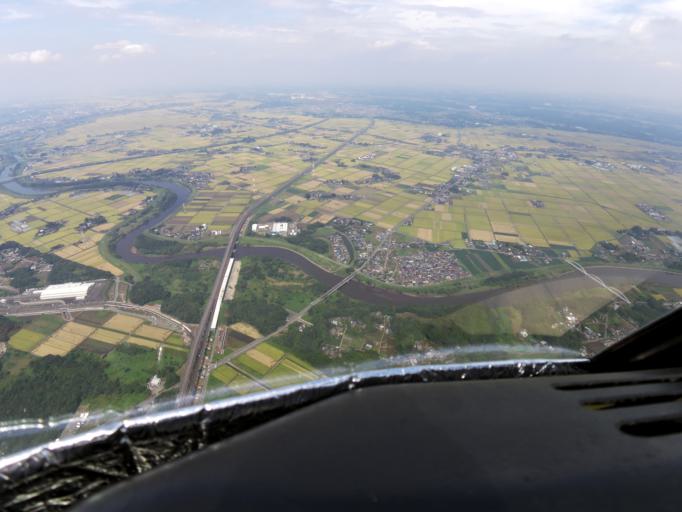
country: JP
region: Ibaraki
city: Moriya
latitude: 35.9526
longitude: 140.0030
